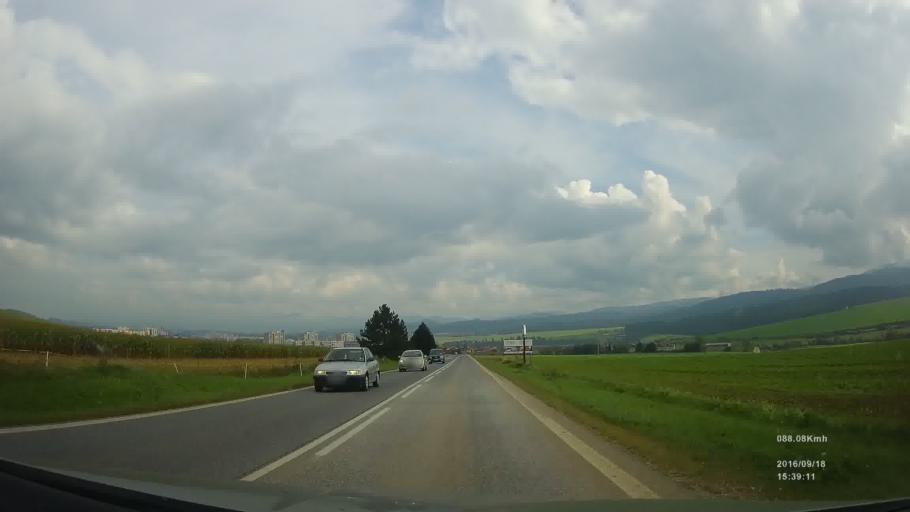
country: SK
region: Kosicky
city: Spisska Nova Ves
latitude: 48.9636
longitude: 20.5029
